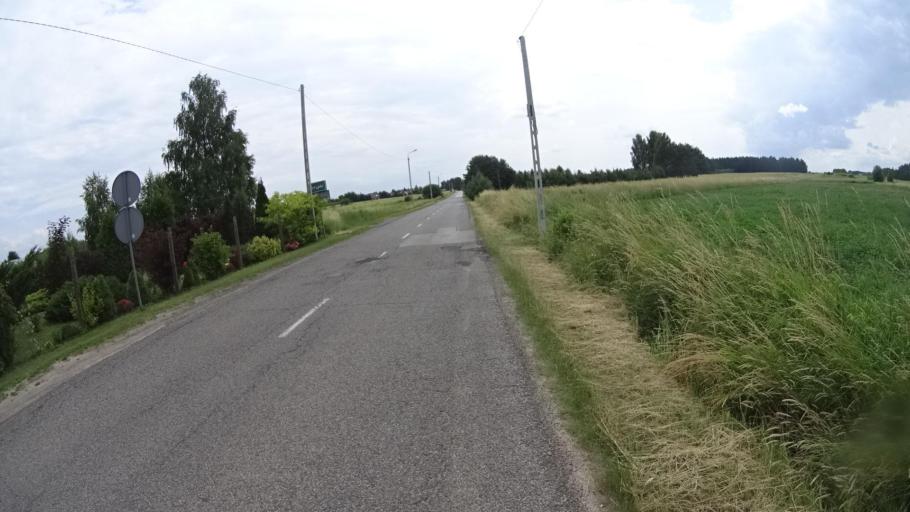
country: PL
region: Masovian Voivodeship
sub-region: Powiat piaseczynski
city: Tarczyn
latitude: 52.0060
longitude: 20.8111
